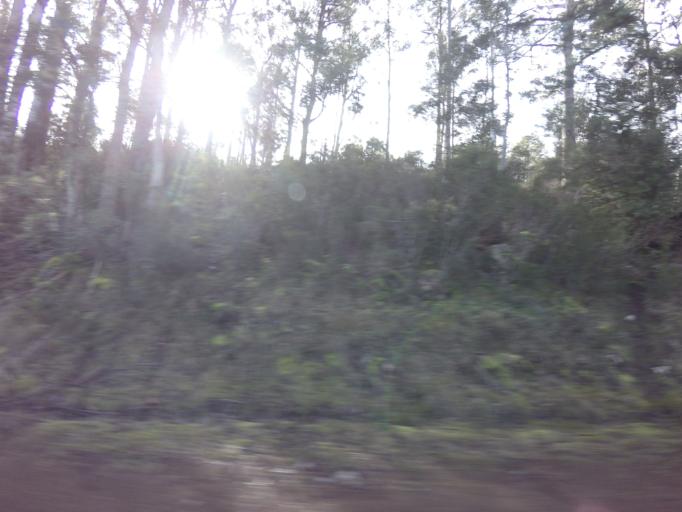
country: AU
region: Tasmania
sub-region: Derwent Valley
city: New Norfolk
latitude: -42.7783
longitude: 146.9002
